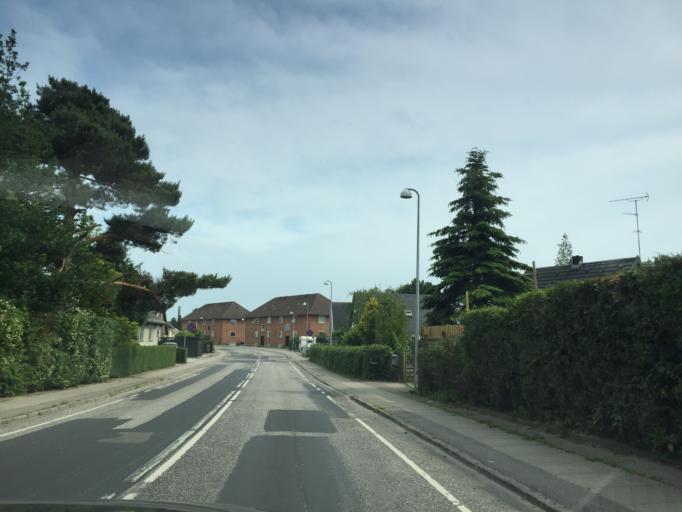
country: DK
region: Capital Region
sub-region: Hoje-Taastrup Kommune
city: Flong
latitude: 55.6543
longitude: 12.1895
